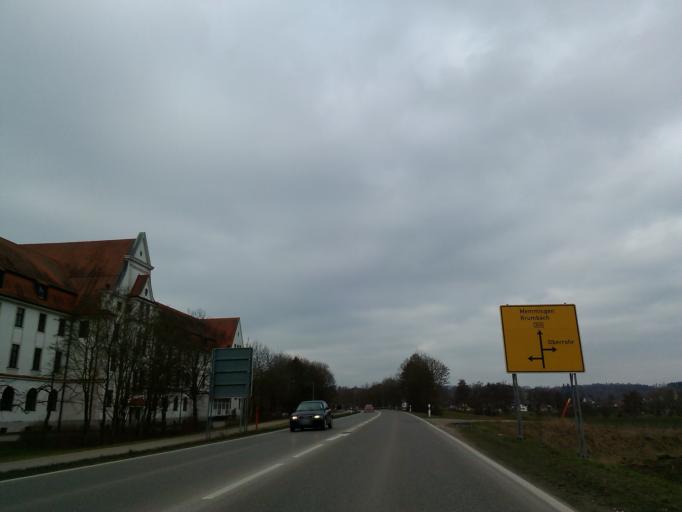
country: DE
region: Bavaria
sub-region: Swabia
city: Ursberg
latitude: 48.2750
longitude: 10.4480
